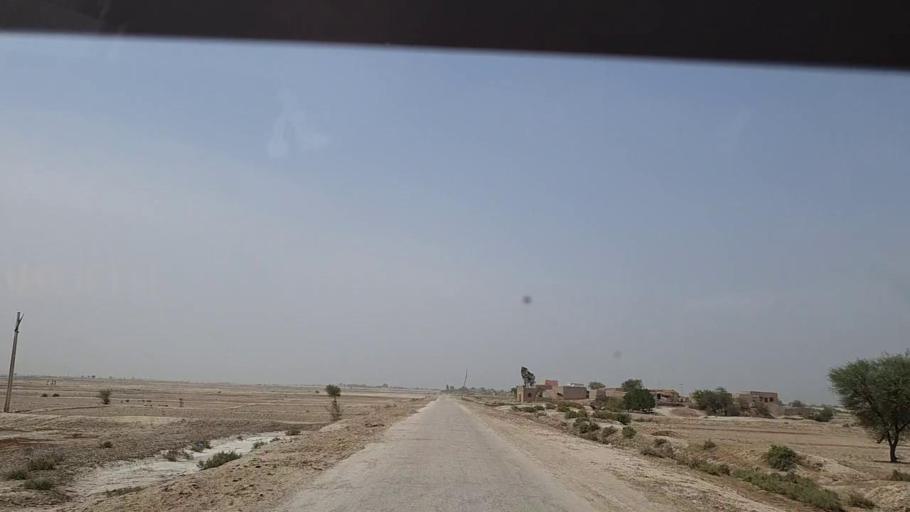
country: PK
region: Sindh
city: Khairpur Nathan Shah
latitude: 27.0619
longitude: 67.6483
